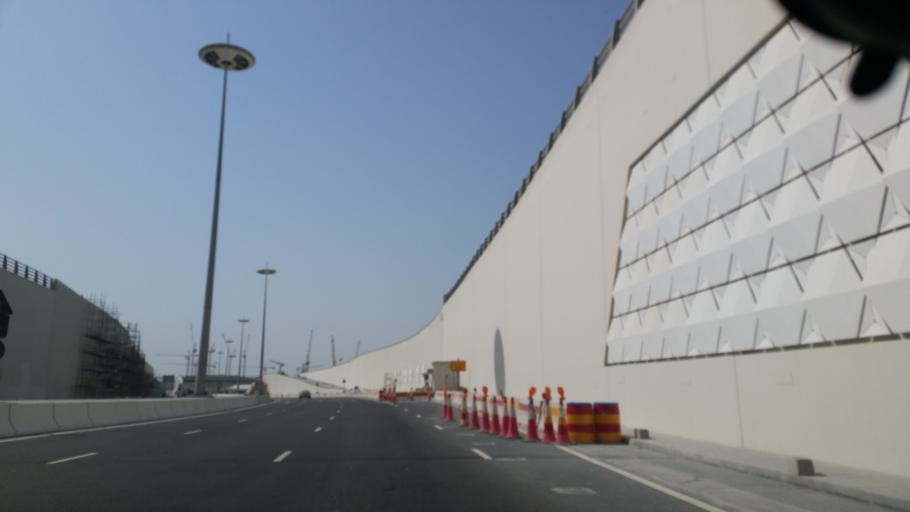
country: QA
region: Baladiyat Umm Salal
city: Umm Salal Muhammad
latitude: 25.4084
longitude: 51.5117
